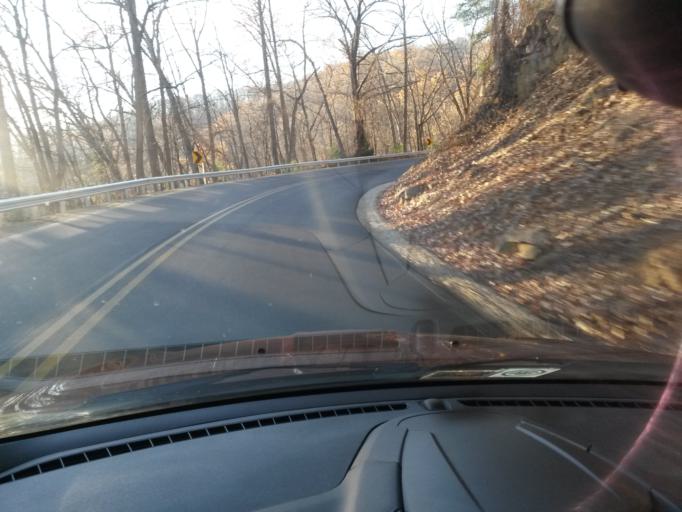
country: US
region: Virginia
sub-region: City of Buena Vista
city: Buena Vista
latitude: 37.7497
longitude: -79.2812
